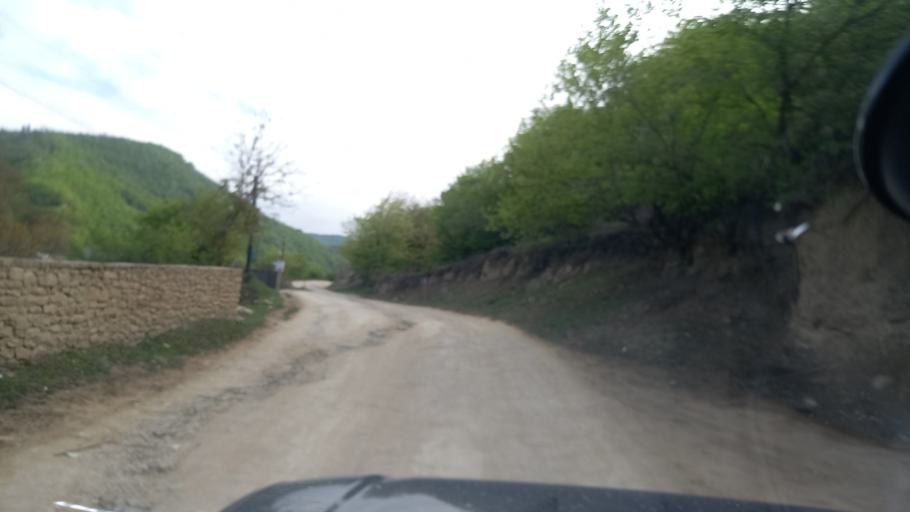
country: RU
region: Dagestan
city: Khuchni
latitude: 41.9705
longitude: 47.8775
